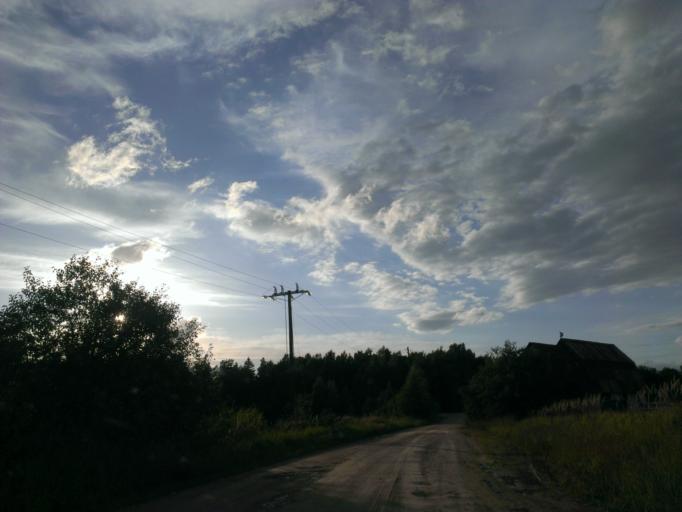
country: LV
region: Ikskile
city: Ikskile
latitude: 56.8532
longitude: 24.5129
